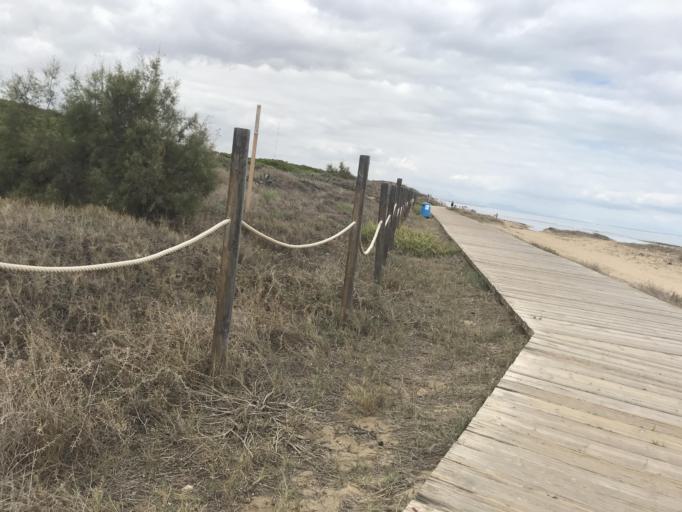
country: ES
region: Valencia
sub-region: Provincia de Alicante
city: Torrevieja
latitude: 38.0298
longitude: -0.6513
